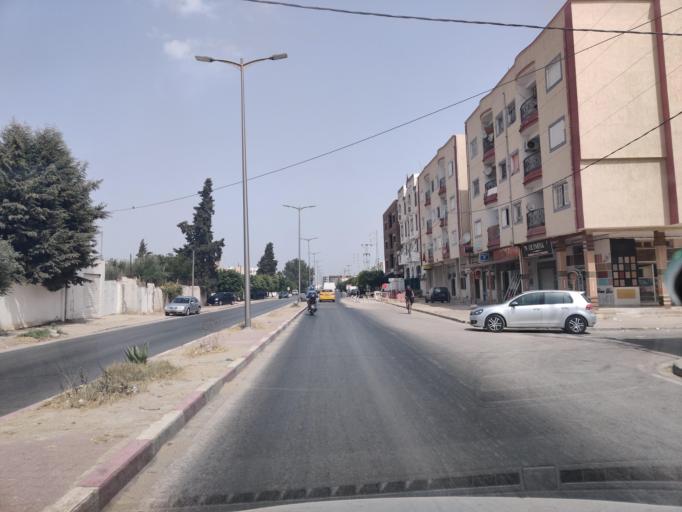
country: TN
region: Nabul
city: Bu `Urqub
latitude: 36.5874
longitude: 10.5063
